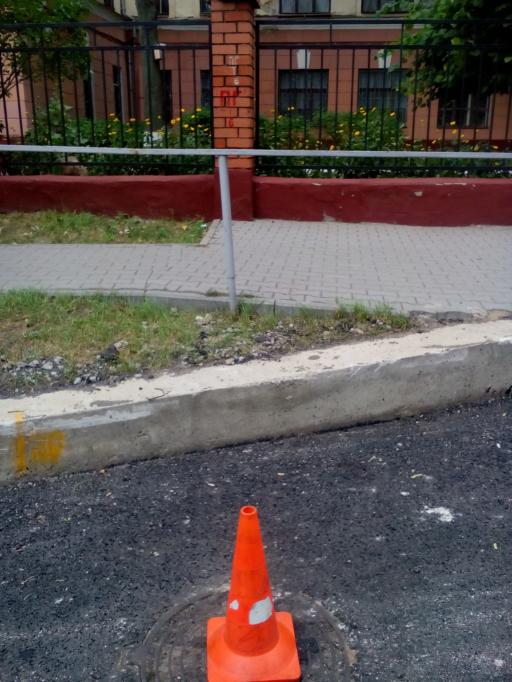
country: RU
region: Voronezj
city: Voronezh
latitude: 51.6674
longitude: 39.2092
